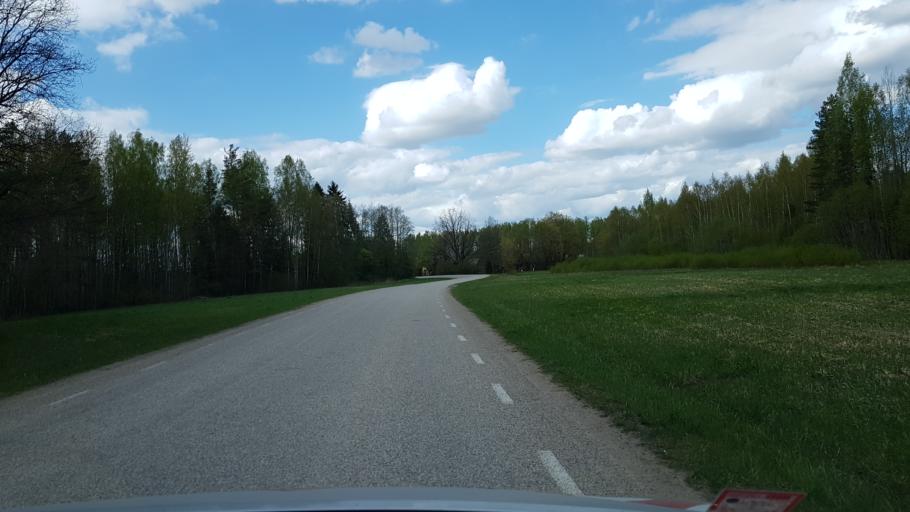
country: EE
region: Tartu
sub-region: Tartu linn
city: Tartu
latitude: 58.3504
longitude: 26.8047
